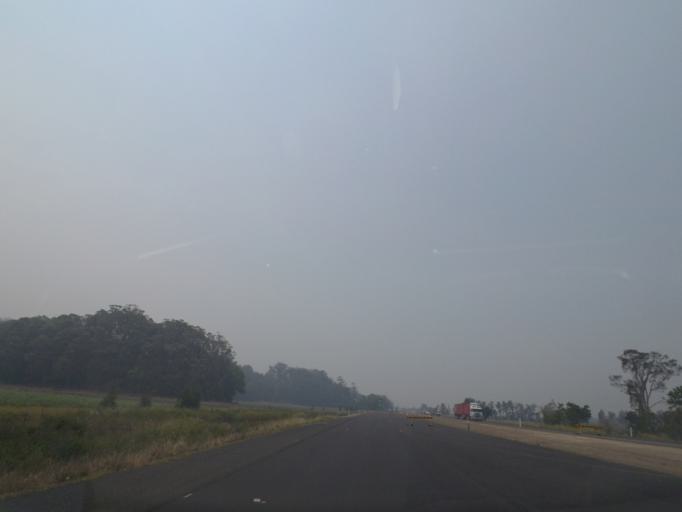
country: AU
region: New South Wales
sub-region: Ballina
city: Ballina
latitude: -28.8840
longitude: 153.4840
